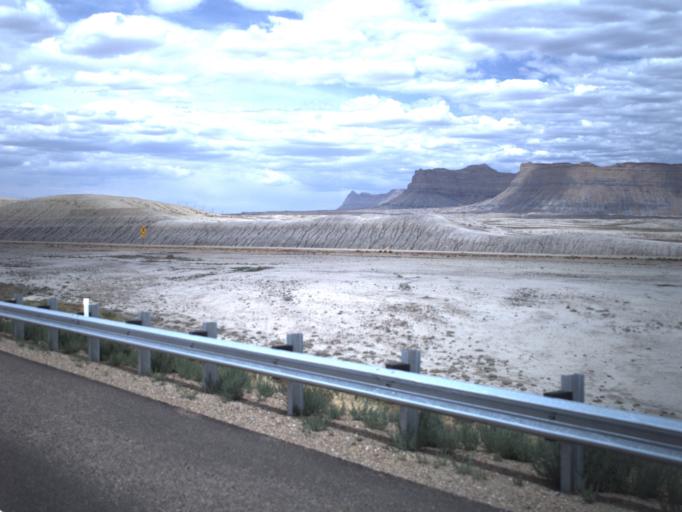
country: US
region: Utah
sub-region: Carbon County
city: East Carbon City
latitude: 38.9826
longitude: -110.2347
